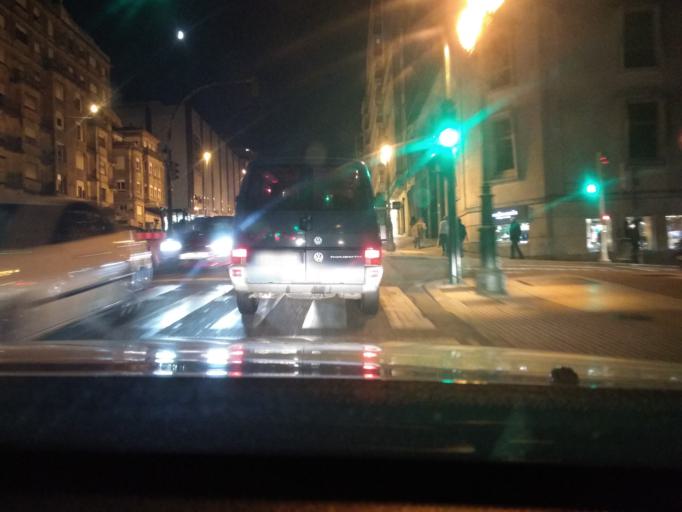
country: ES
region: Galicia
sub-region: Provincia de Pontevedra
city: Vigo
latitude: 42.2338
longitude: -8.7172
